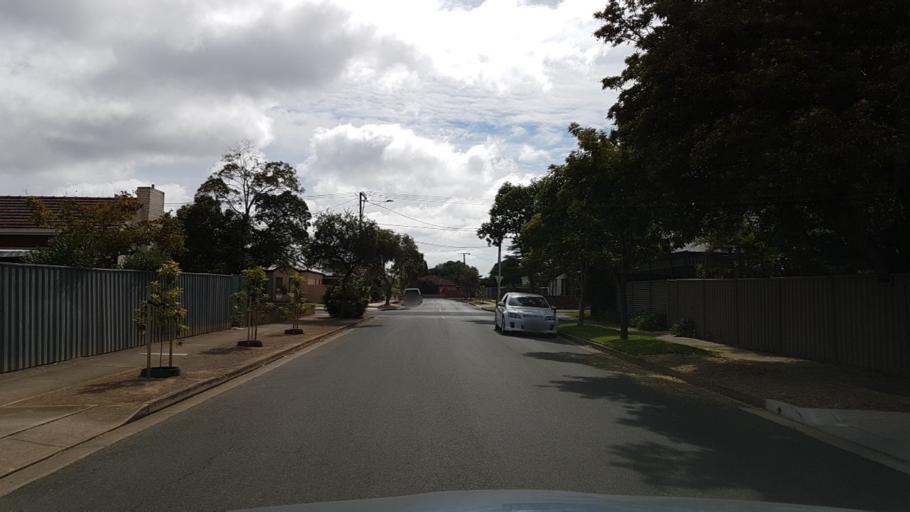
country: AU
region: South Australia
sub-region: Marion
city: South Plympton
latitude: -34.9743
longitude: 138.5514
